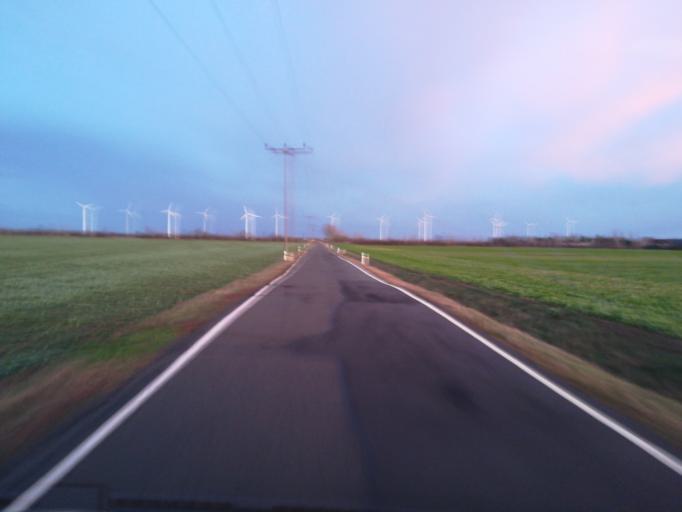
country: DE
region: Saxony-Anhalt
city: Roitzsch
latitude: 51.5567
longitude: 12.2668
